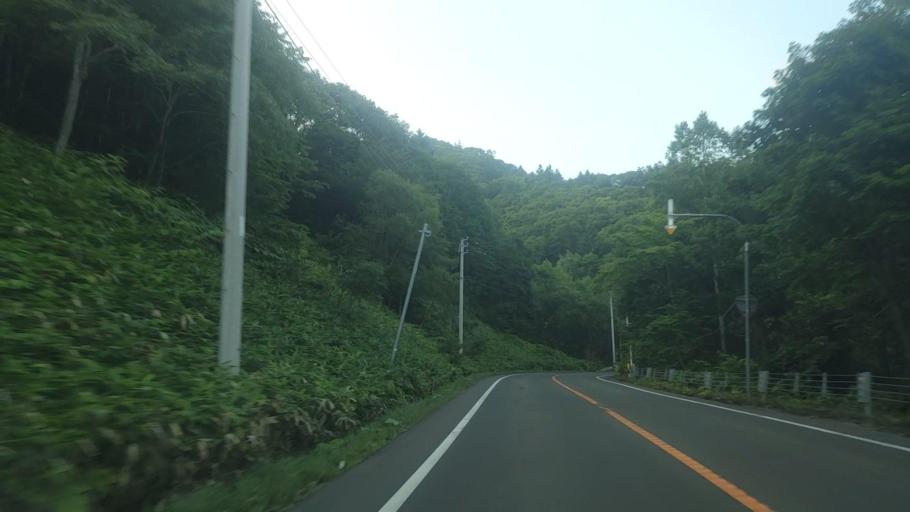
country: JP
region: Hokkaido
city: Bibai
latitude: 43.2673
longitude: 142.0326
